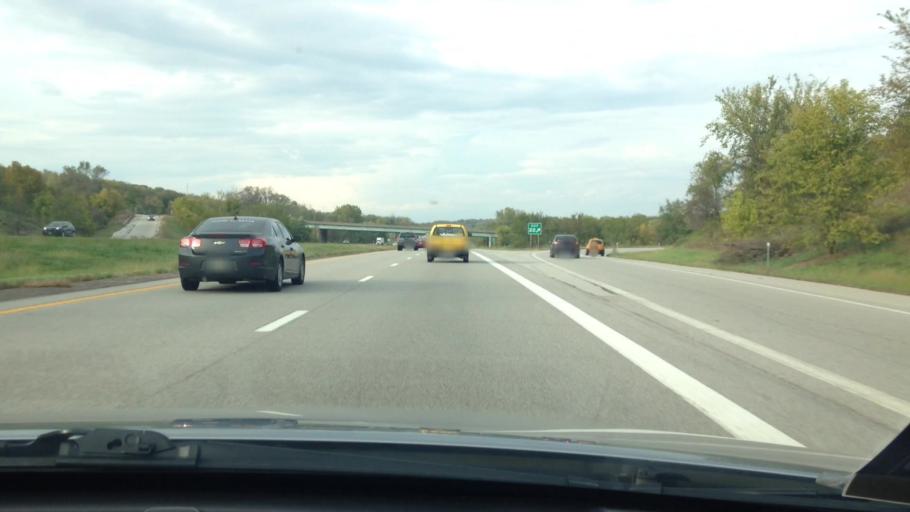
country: US
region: Missouri
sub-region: Platte County
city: Weatherby Lake
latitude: 39.2213
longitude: -94.7628
